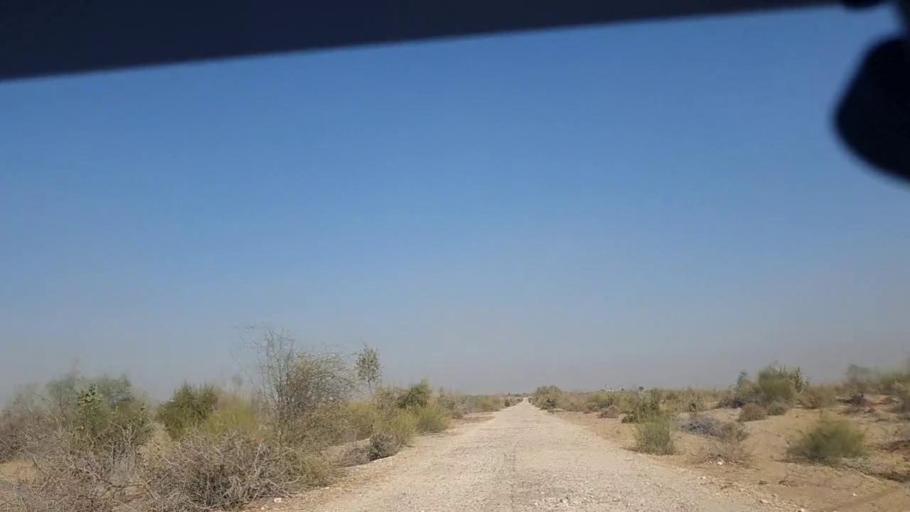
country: PK
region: Sindh
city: Khanpur
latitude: 27.5702
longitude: 69.3442
